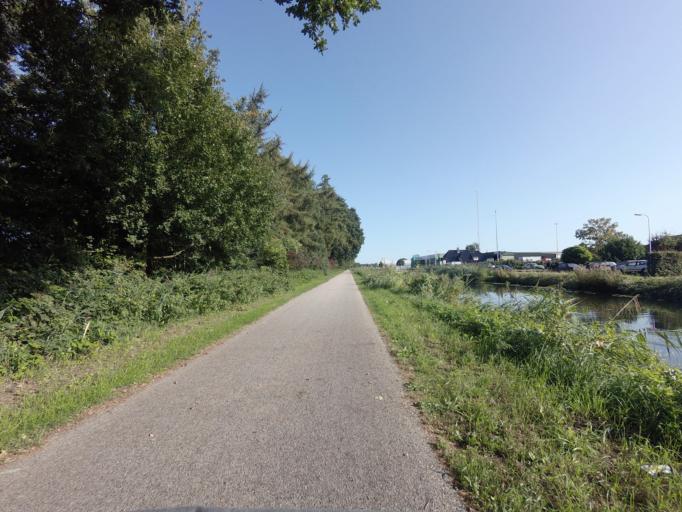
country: NL
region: Overijssel
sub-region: Gemeente Raalte
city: Raalte
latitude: 52.3777
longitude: 6.2782
